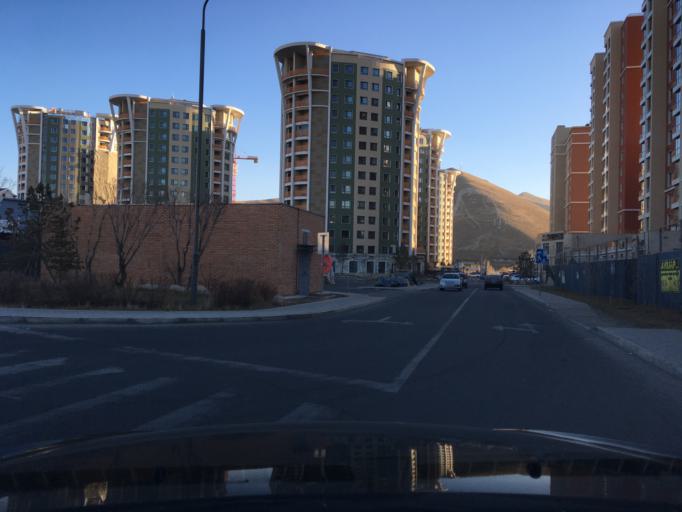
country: MN
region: Ulaanbaatar
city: Ulaanbaatar
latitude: 47.8923
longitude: 106.9258
